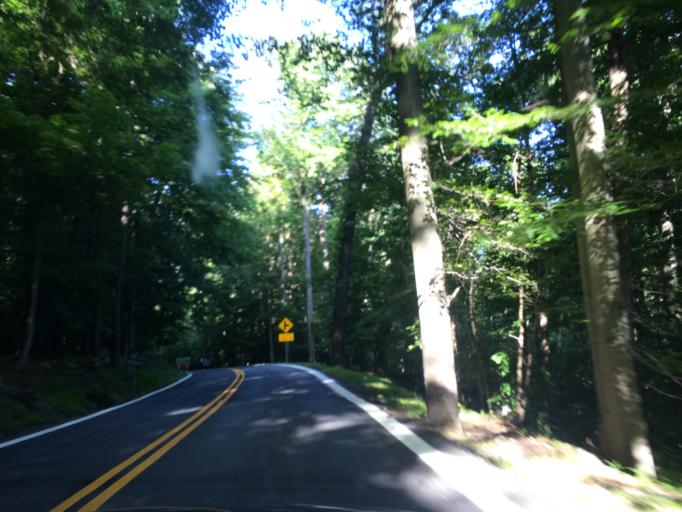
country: US
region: Maryland
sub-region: Frederick County
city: Thurmont
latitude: 39.6328
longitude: -77.4560
